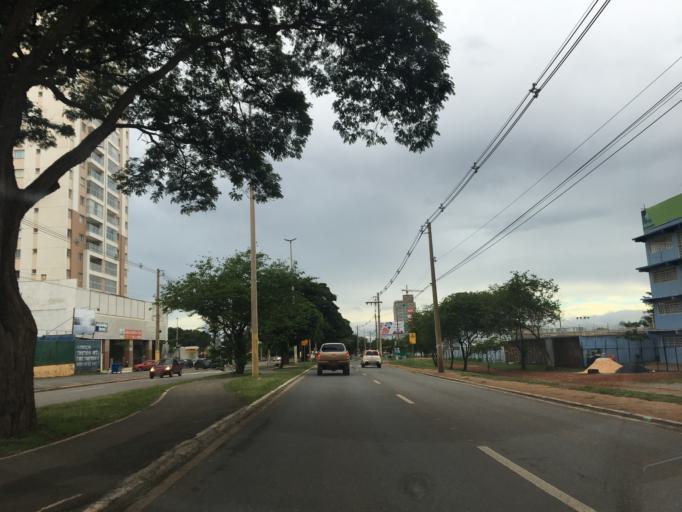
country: BR
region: Goias
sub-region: Luziania
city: Luziania
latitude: -16.0145
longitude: -48.0602
